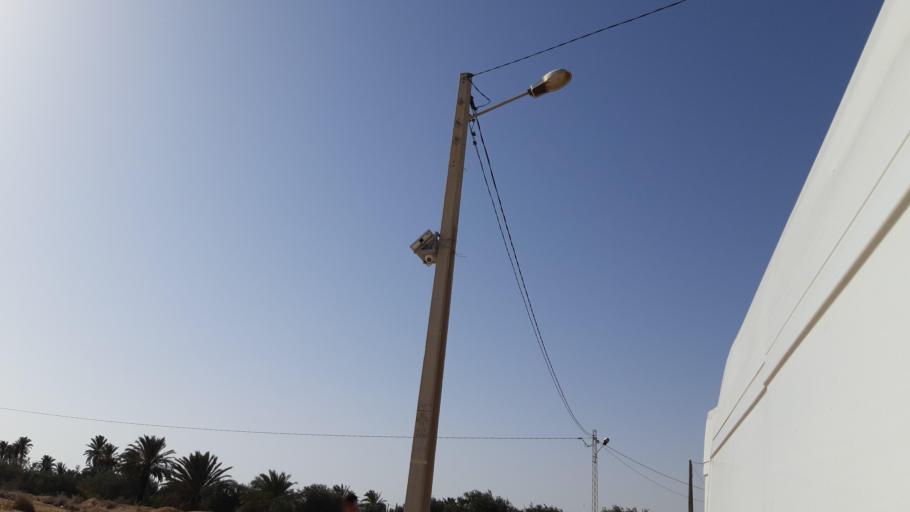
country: TN
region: Qabis
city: Gabes
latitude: 33.8074
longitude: 10.0790
